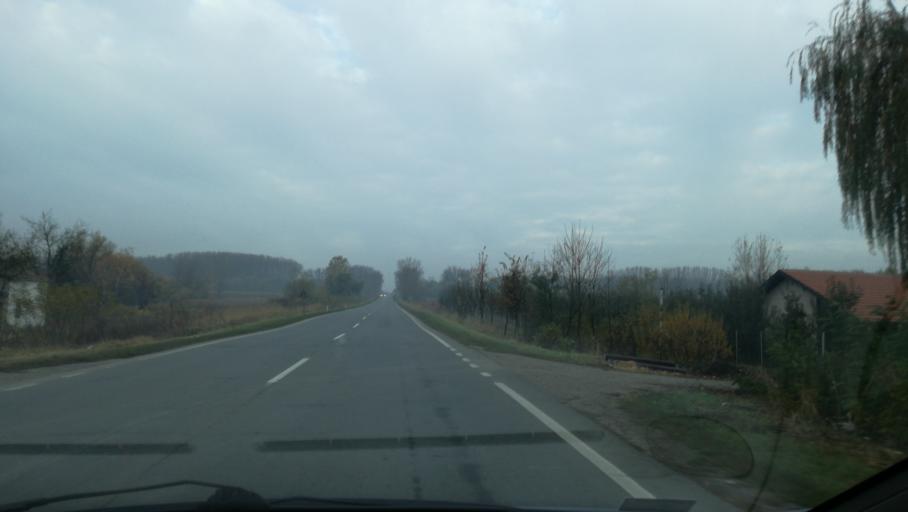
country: RS
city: Aradac
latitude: 45.3922
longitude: 20.2246
